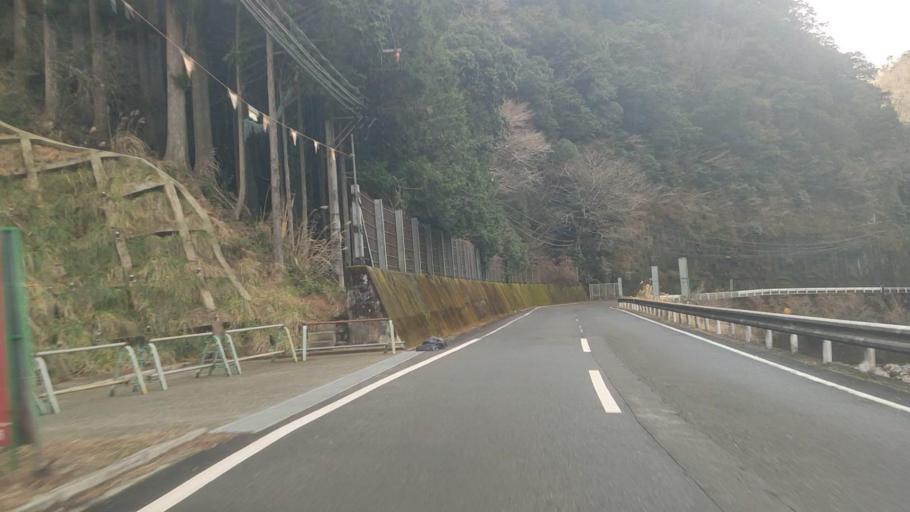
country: JP
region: Kumamoto
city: Hitoyoshi
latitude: 32.4253
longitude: 130.8569
